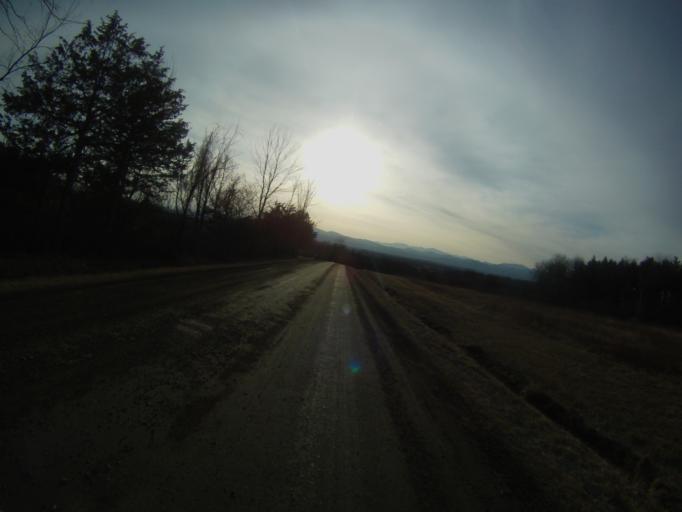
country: US
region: Vermont
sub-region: Addison County
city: Middlebury (village)
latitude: 44.0397
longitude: -73.2895
